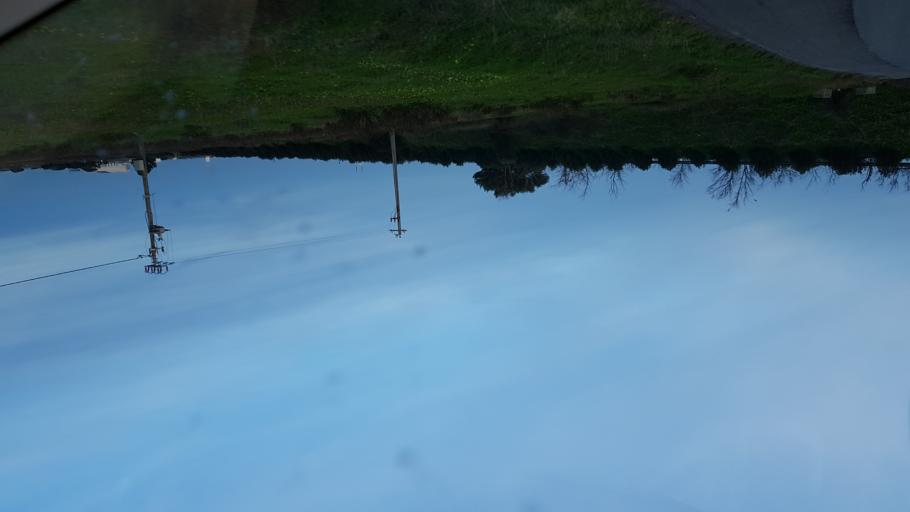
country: IT
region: Apulia
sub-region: Provincia di Brindisi
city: Brindisi
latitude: 40.6588
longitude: 17.9116
